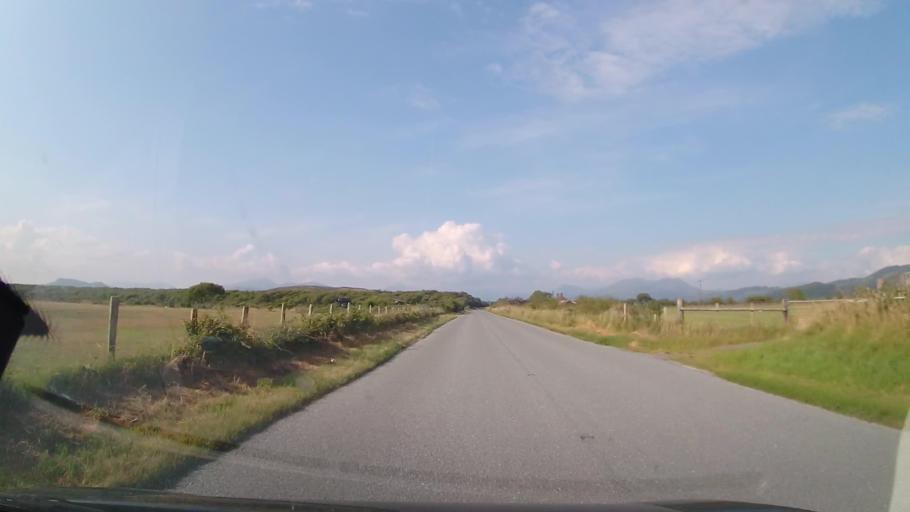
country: GB
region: Wales
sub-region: Gwynedd
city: Llanfair
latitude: 52.8747
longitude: -4.1048
